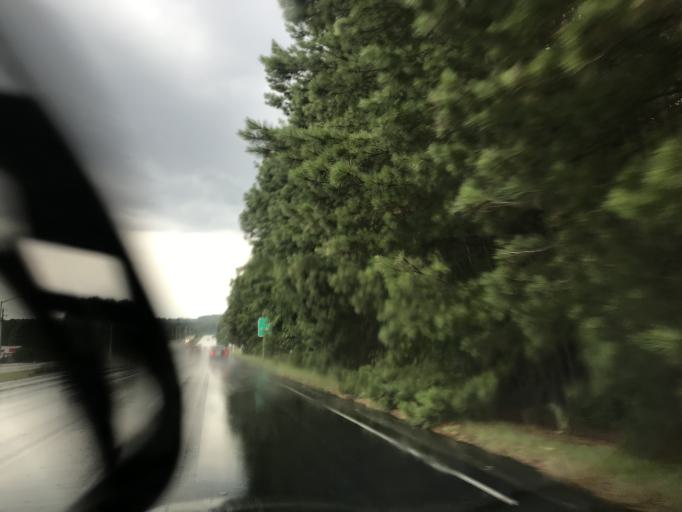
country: US
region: North Carolina
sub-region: Johnston County
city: Clayton
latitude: 35.6440
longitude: -78.4564
